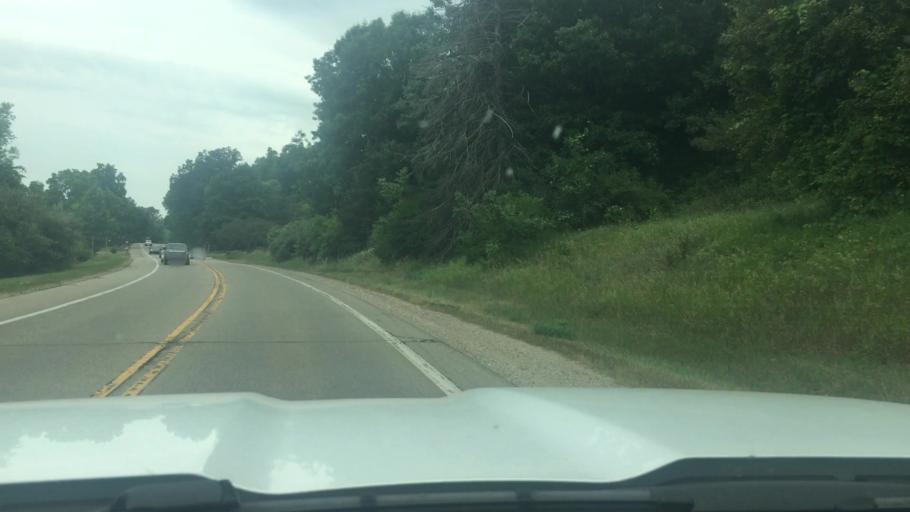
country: US
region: Michigan
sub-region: Ionia County
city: Saranac
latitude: 42.9552
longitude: -85.1750
